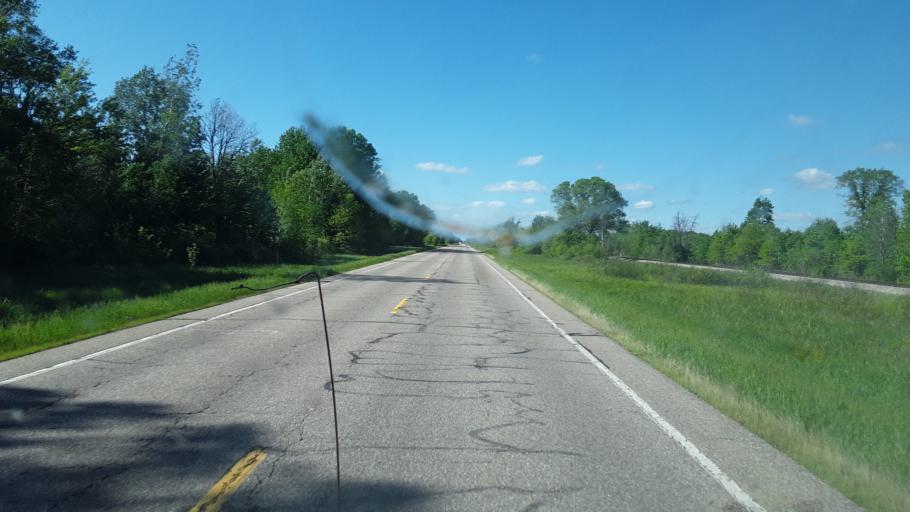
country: US
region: Wisconsin
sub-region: Wood County
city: Nekoosa
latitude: 44.1746
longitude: -90.1338
